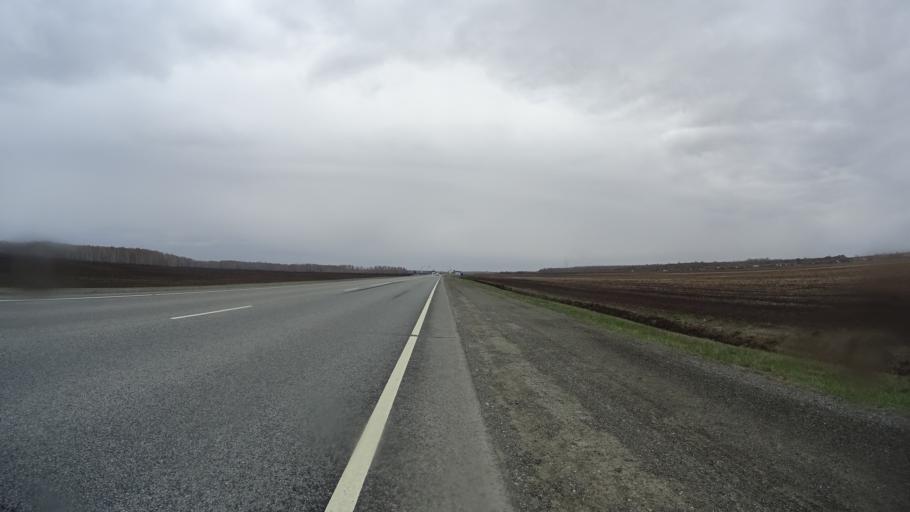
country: RU
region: Chelyabinsk
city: Krasnogorskiy
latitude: 54.5847
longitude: 61.2909
